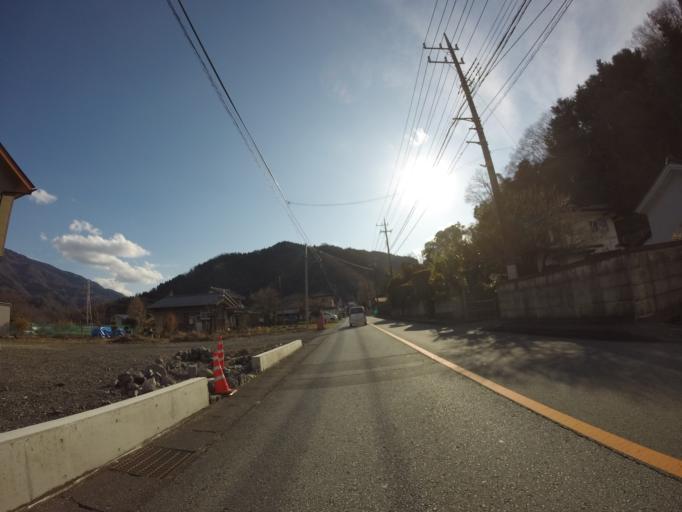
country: JP
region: Shizuoka
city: Fujinomiya
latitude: 35.3734
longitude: 138.4445
